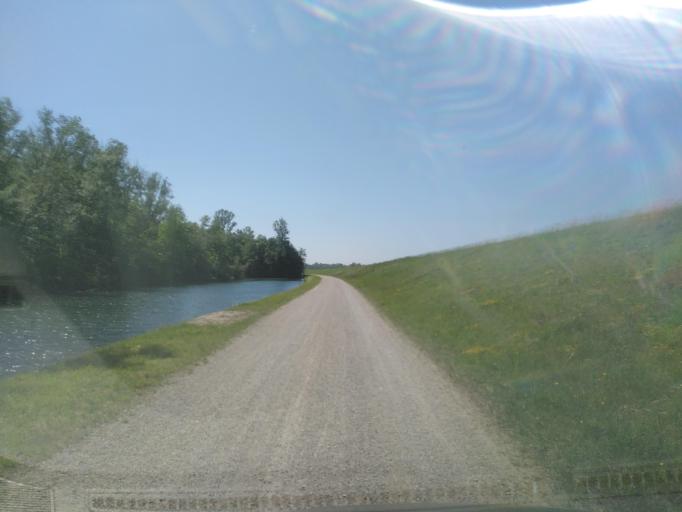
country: FR
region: Alsace
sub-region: Departement du Haut-Rhin
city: Kunheim
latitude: 48.0890
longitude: 7.5741
